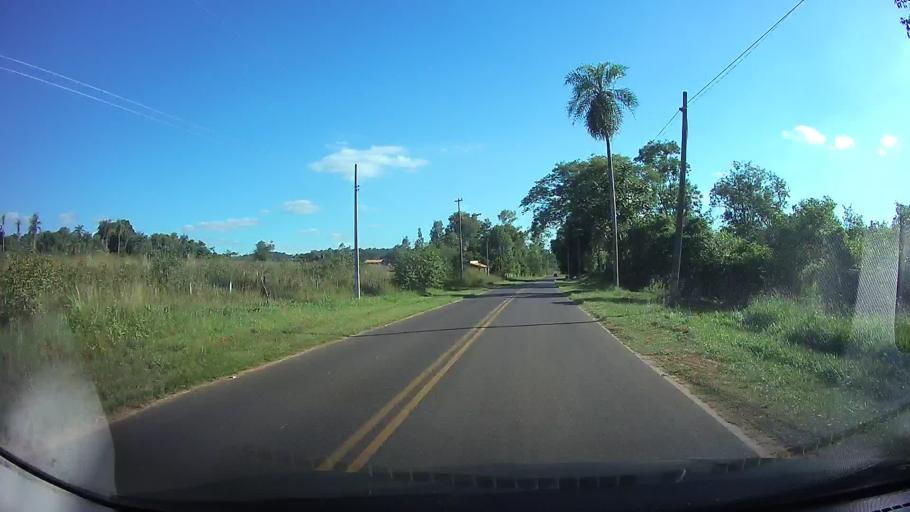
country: PY
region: Cordillera
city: Atyra
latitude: -25.2994
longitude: -57.1851
